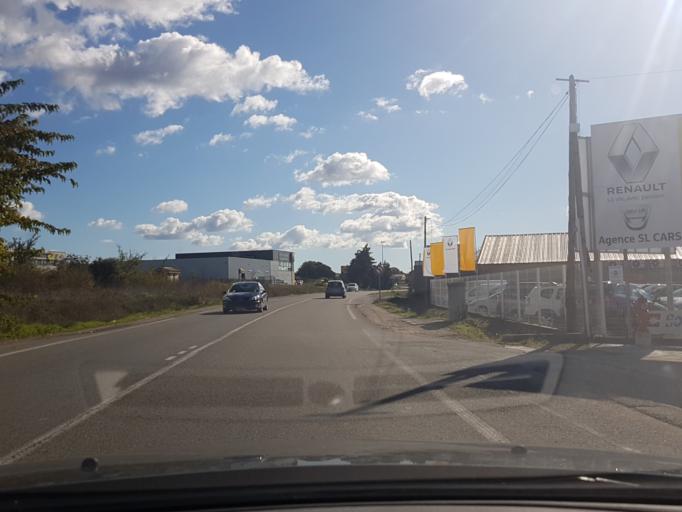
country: FR
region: Provence-Alpes-Cote d'Azur
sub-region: Departement du Vaucluse
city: Morieres-les-Avignon
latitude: 43.9565
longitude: 4.9009
